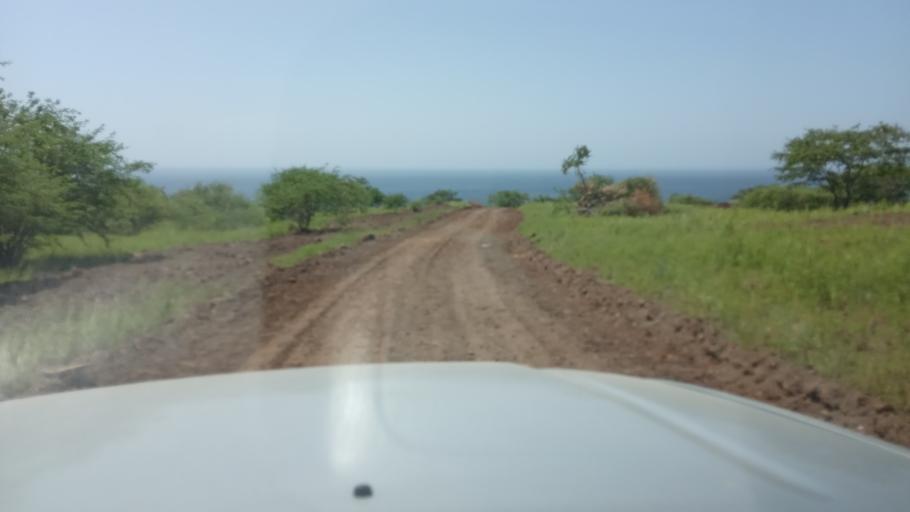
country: CV
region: Santa Catarina
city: Assomada
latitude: 15.1201
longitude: -23.7631
